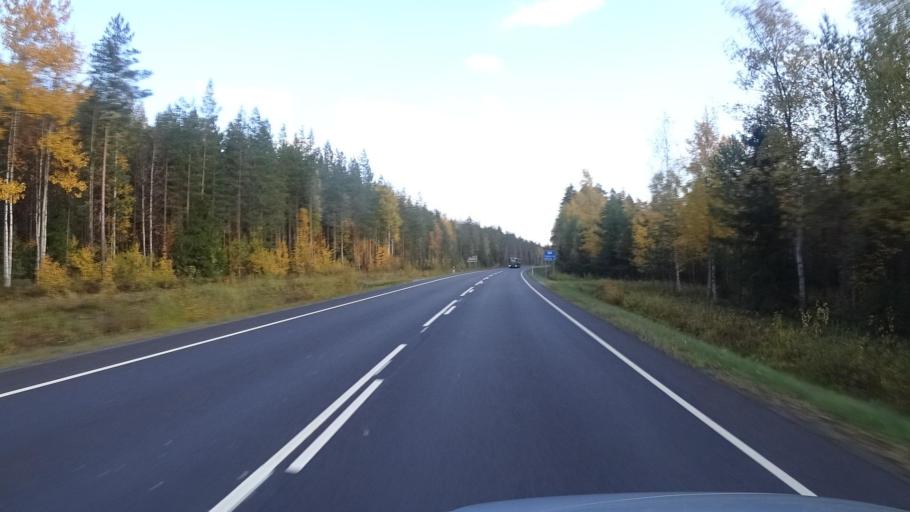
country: FI
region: Satakunta
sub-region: Rauma
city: Koeylioe
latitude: 61.1048
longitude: 22.2274
